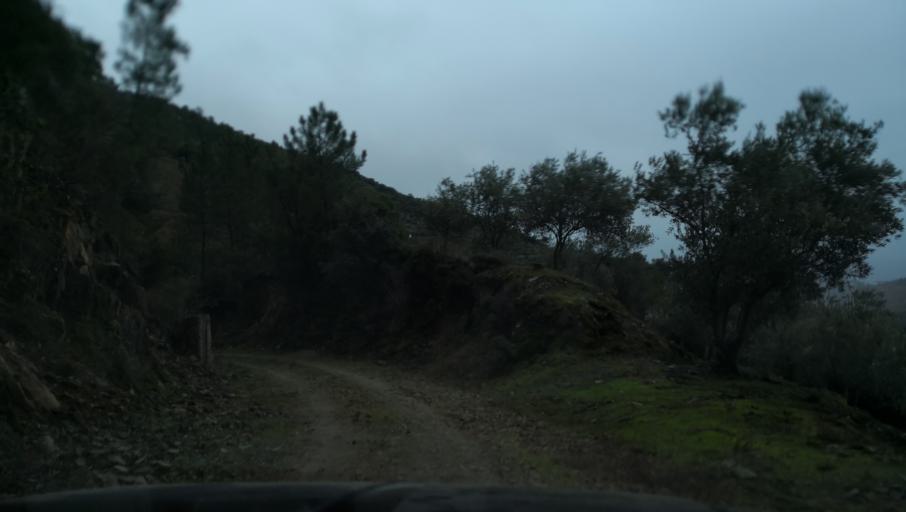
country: PT
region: Vila Real
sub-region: Vila Real
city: Vila Real
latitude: 41.2561
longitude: -7.7449
